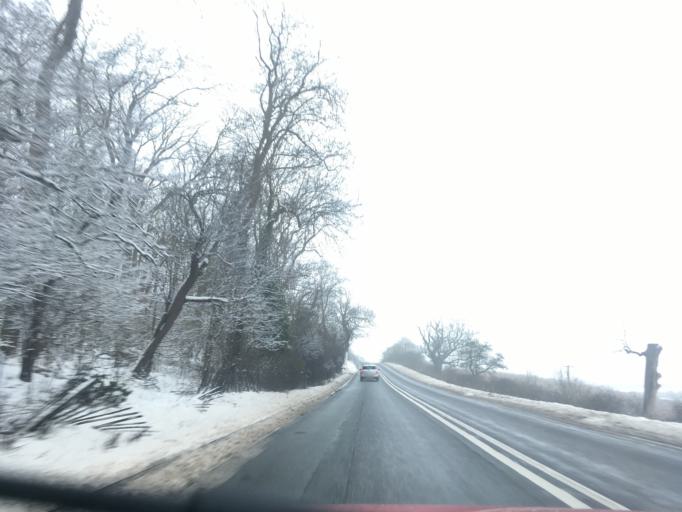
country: GB
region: England
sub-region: Warwickshire
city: Stratford-upon-Avon
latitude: 52.2000
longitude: -1.7687
